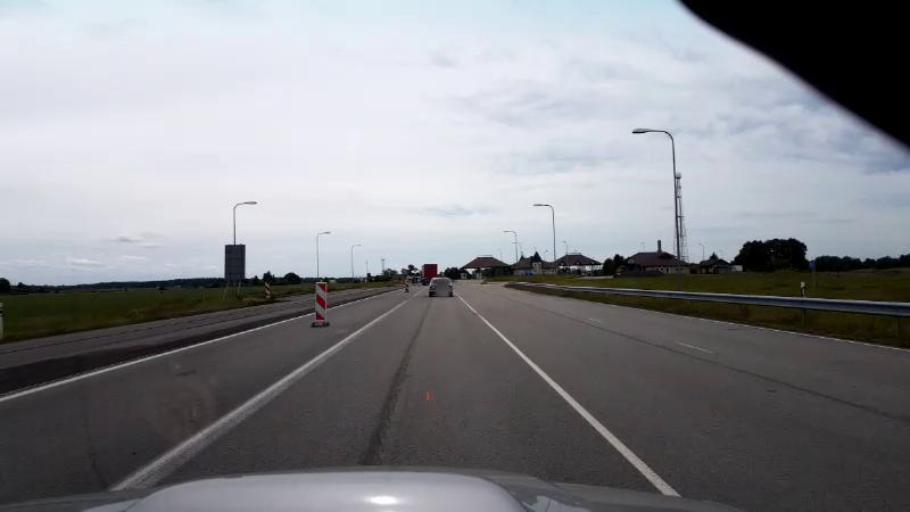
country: LV
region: Bauskas Rajons
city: Bauska
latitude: 56.2778
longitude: 24.3633
